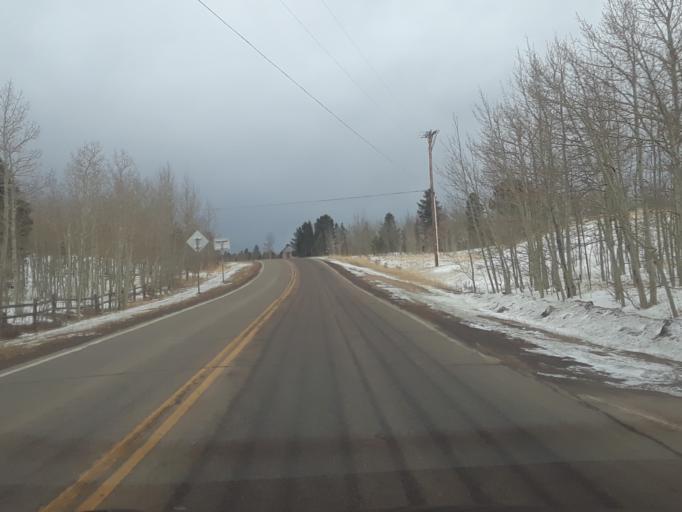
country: US
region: Colorado
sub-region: Gilpin County
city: Central City
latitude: 39.8395
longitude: -105.4806
